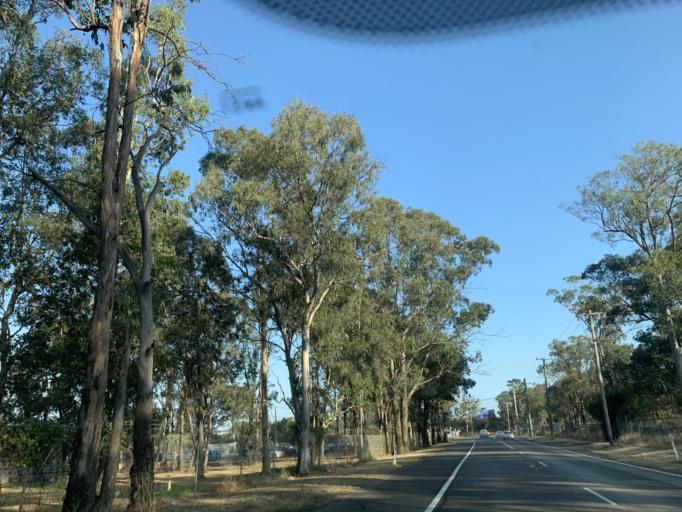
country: AU
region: New South Wales
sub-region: Fairfield
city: Horsley Park
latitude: -33.8252
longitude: 150.8713
